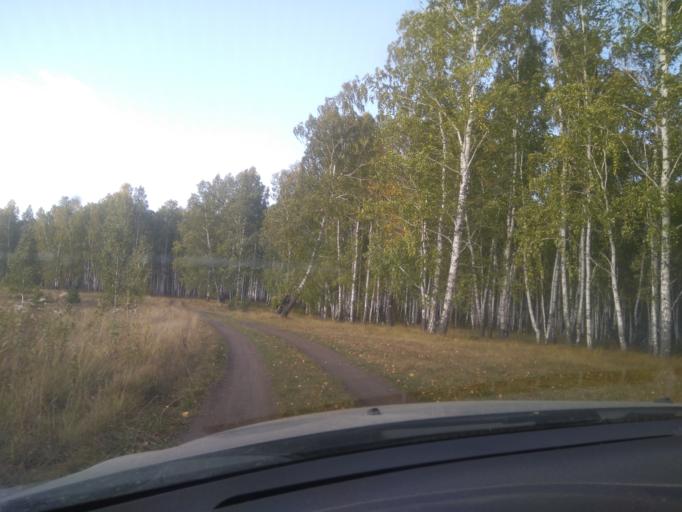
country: RU
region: Sverdlovsk
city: Pokrovskoye
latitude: 56.4288
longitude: 61.6097
